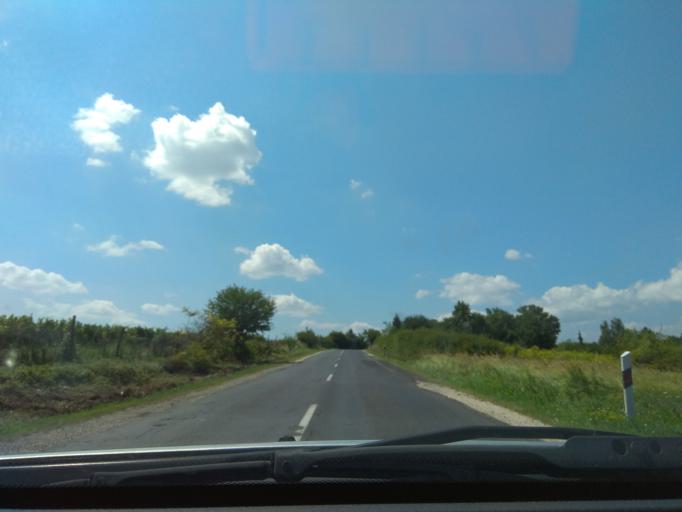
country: HU
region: Borsod-Abauj-Zemplen
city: Malyi
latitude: 48.0386
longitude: 20.7827
